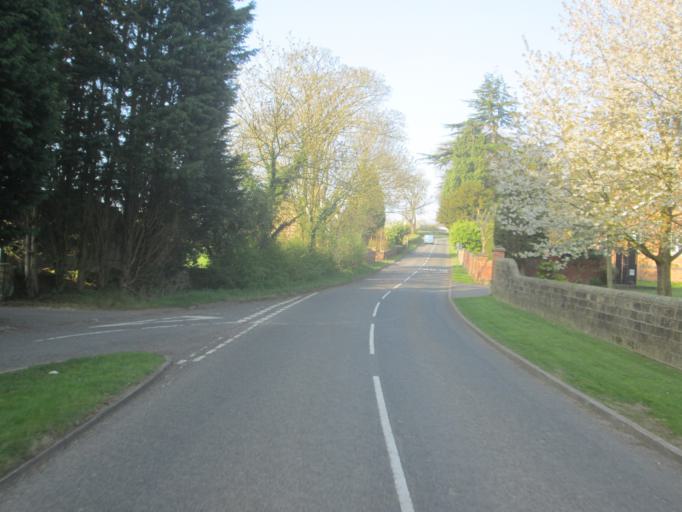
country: GB
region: England
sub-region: Derbyshire
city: Wirksworth
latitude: 53.0228
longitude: -1.5653
